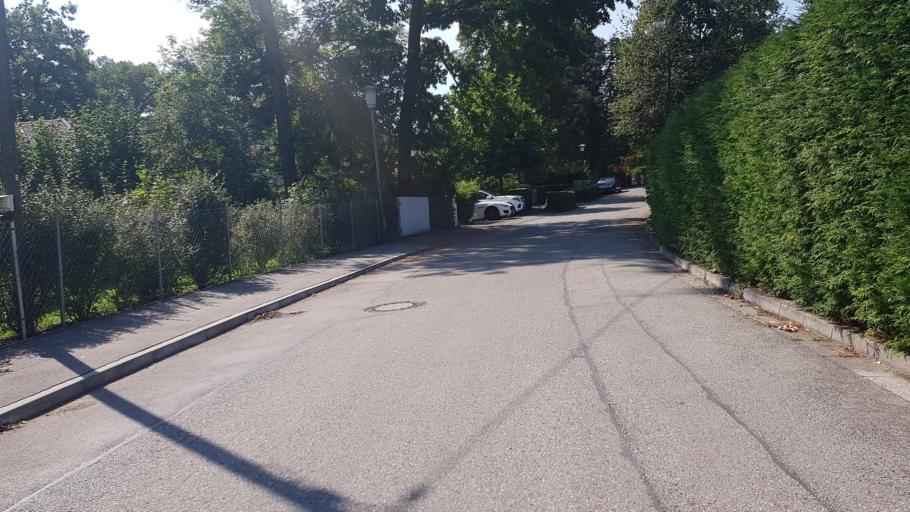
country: DE
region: Bavaria
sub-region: Upper Bavaria
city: Seefeld
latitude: 48.0355
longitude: 11.1940
